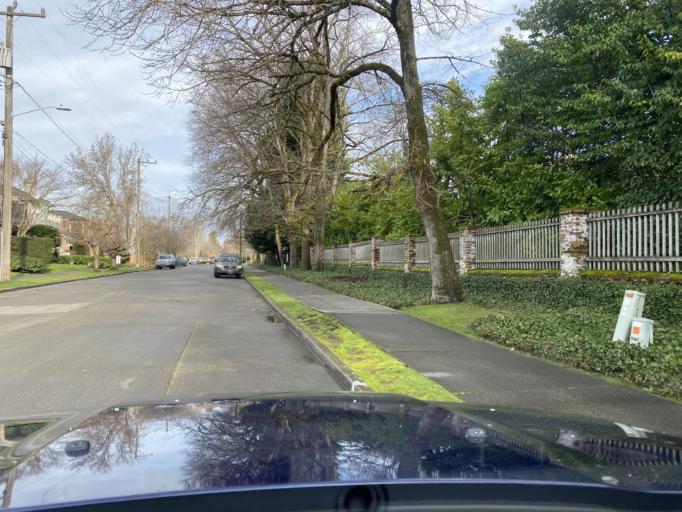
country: US
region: Washington
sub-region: King County
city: Medina
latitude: 47.6324
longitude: -122.2785
